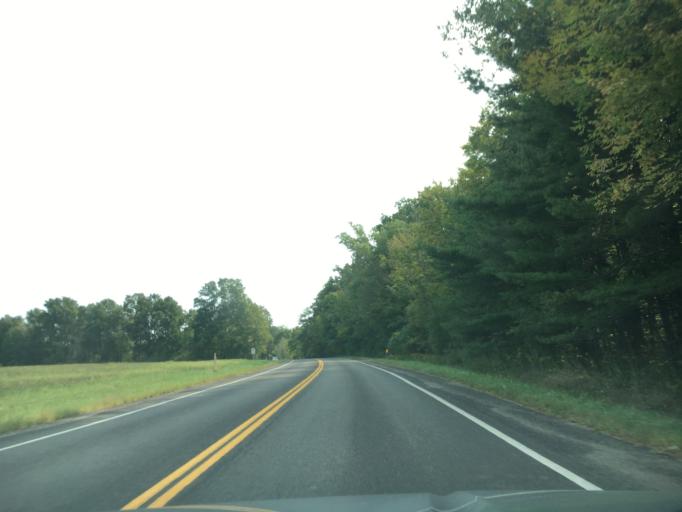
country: US
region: New York
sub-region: Steuben County
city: Sylvan Beach
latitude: 42.4767
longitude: -77.1224
